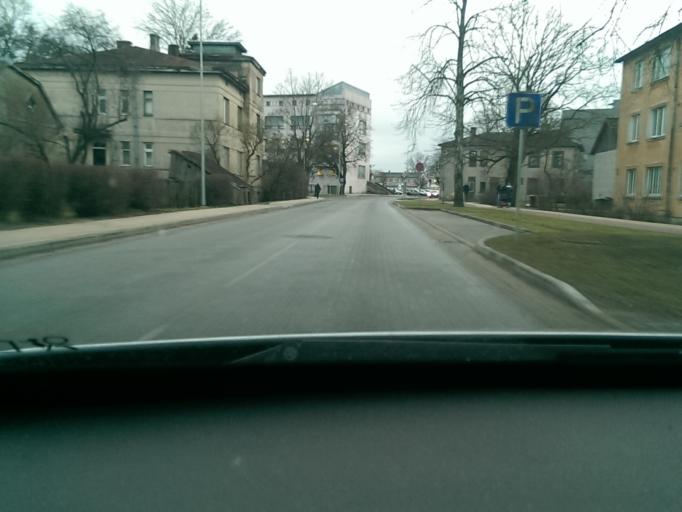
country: LV
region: Kuldigas Rajons
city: Kuldiga
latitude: 56.9707
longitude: 21.9597
